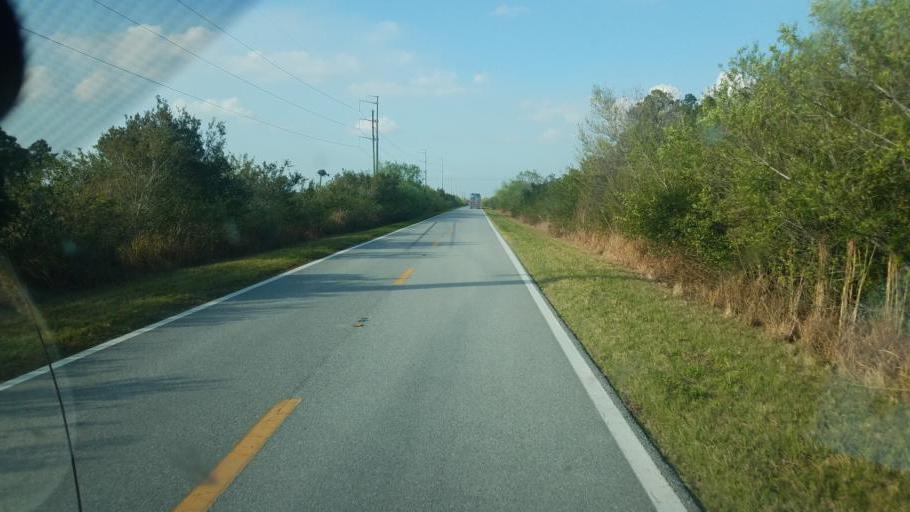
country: US
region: Florida
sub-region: Hardee County
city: Bowling Green
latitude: 27.6585
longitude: -81.9511
